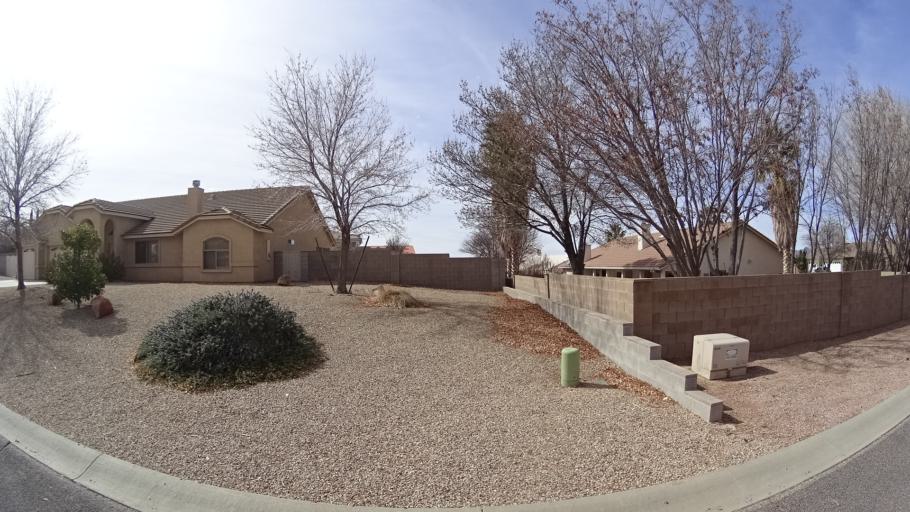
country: US
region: Arizona
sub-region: Mohave County
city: Kingman
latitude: 35.1919
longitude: -113.9790
